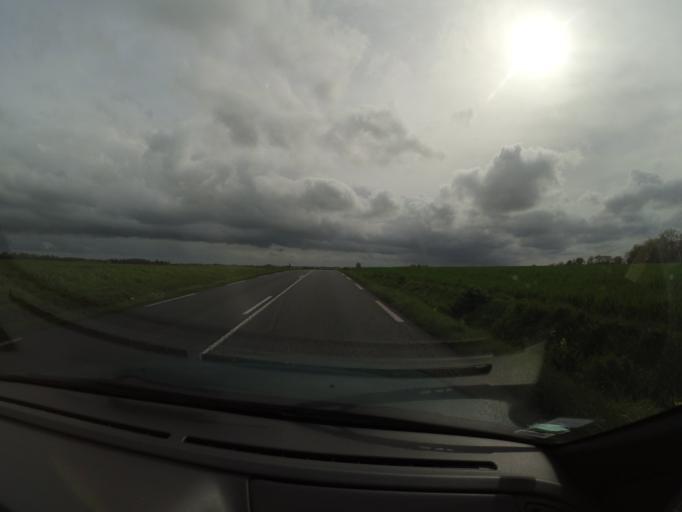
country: FR
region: Pays de la Loire
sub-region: Departement de Maine-et-Loire
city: Landemont
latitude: 47.2528
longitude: -1.2062
